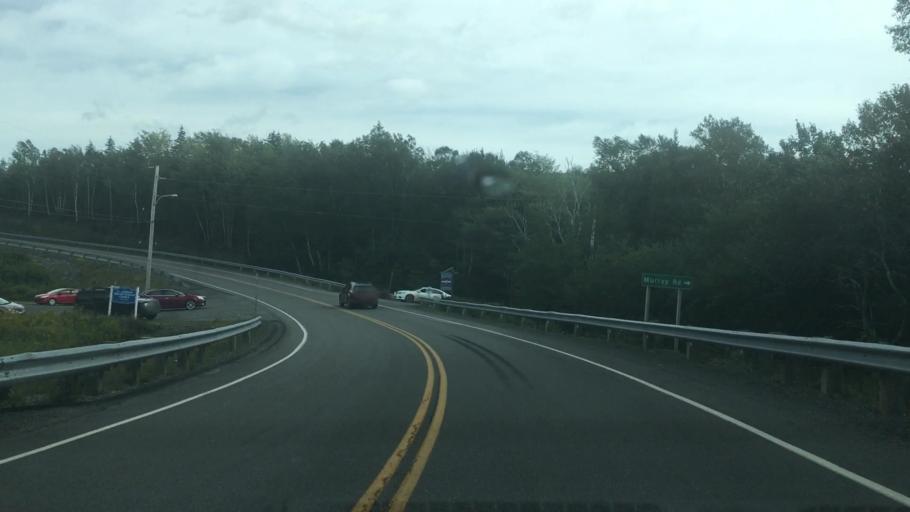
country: CA
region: Nova Scotia
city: Sydney Mines
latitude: 46.3077
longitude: -60.6188
